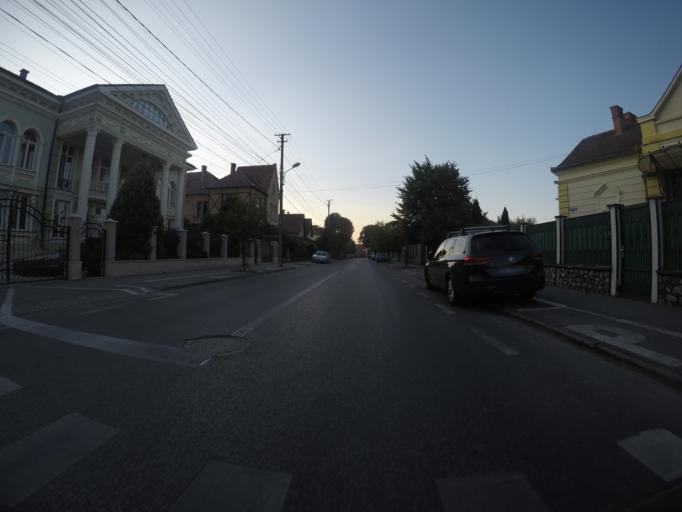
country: RO
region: Sibiu
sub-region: Municipiul Sibiu
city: Sibiu
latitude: 45.7908
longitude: 24.1576
